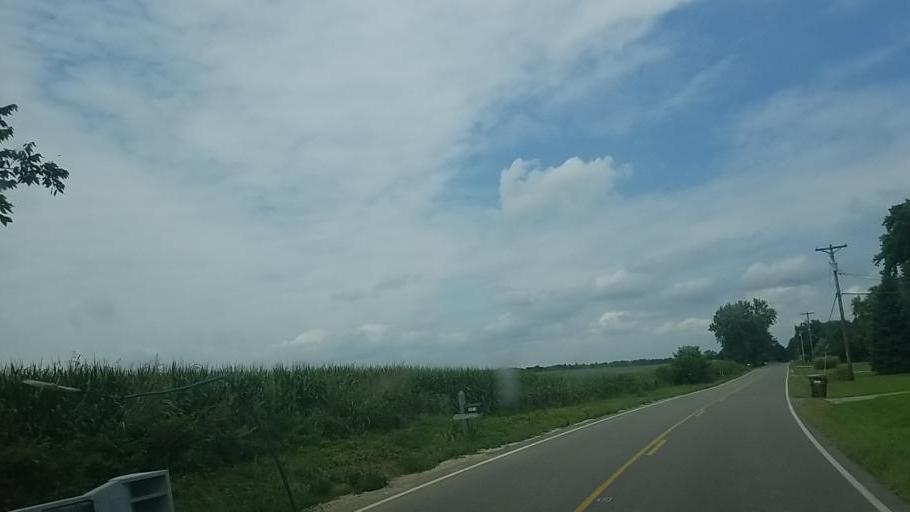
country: US
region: Ohio
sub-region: Pickaway County
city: Ashville
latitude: 39.7714
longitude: -82.9115
